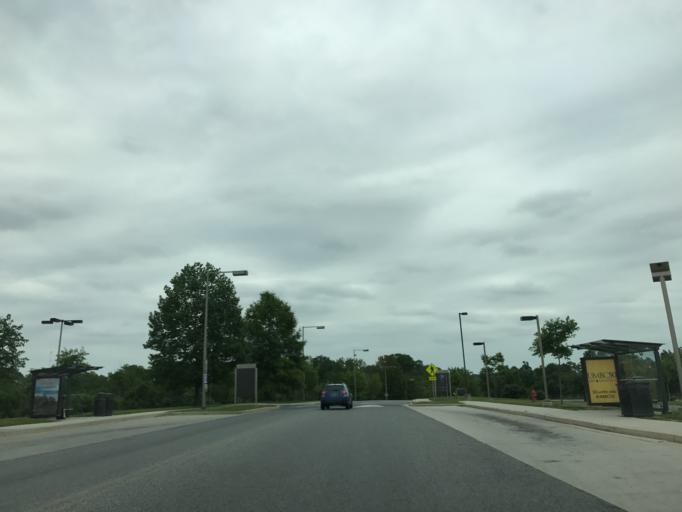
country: US
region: Maryland
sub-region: Baltimore County
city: Arbutus
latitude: 39.2545
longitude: -76.7060
